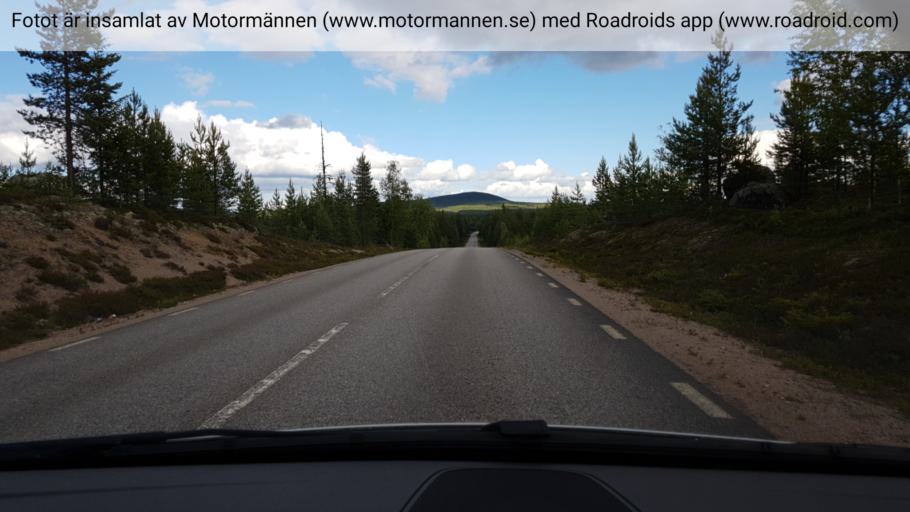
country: SE
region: Jaemtland
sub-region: Harjedalens Kommun
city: Sveg
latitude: 61.9961
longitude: 14.9834
